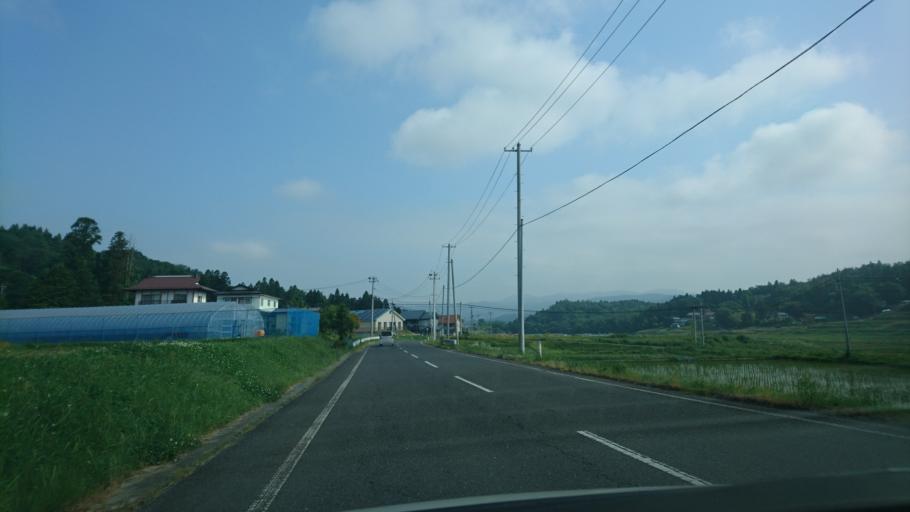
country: JP
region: Iwate
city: Ichinoseki
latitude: 38.9274
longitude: 141.1724
